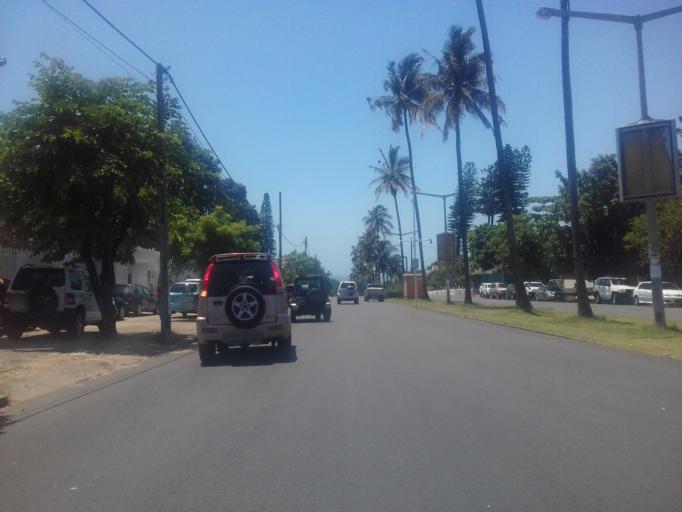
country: MZ
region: Maputo City
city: Maputo
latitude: -25.9587
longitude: 32.5995
